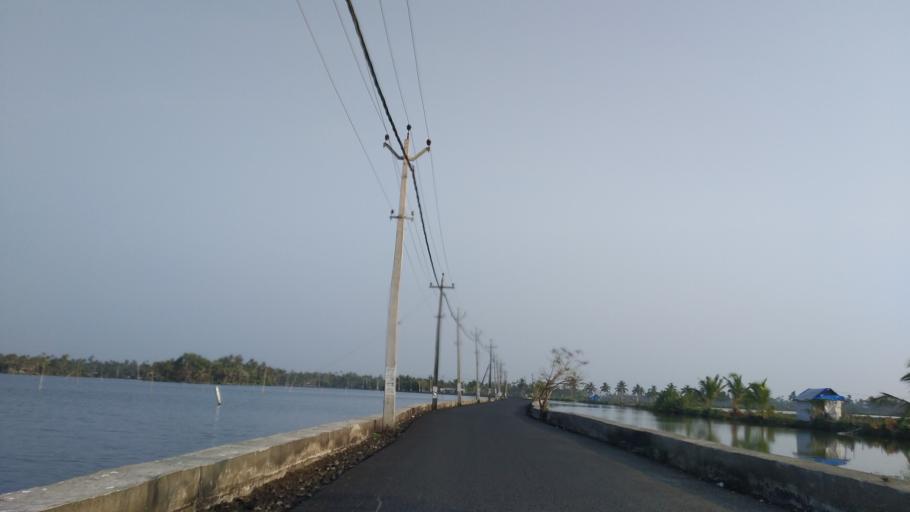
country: IN
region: Kerala
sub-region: Ernakulam
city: Elur
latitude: 10.1095
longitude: 76.1903
